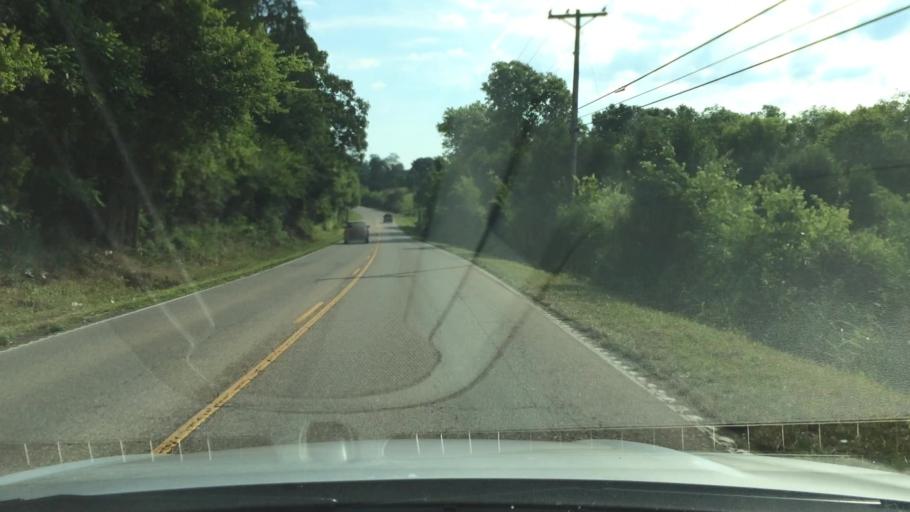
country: US
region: Tennessee
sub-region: Sevier County
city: Seymour
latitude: 35.9007
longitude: -83.7033
